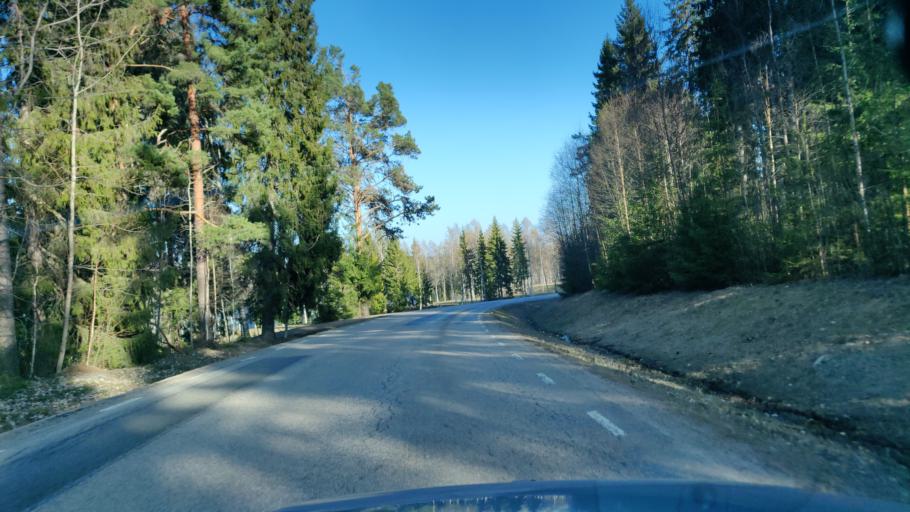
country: SE
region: Vaermland
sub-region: Munkfors Kommun
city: Munkfors
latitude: 59.9695
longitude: 13.4613
